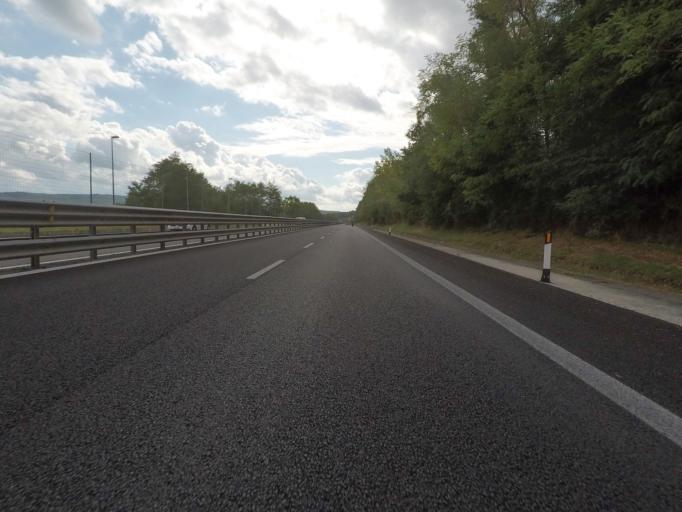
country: IT
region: Tuscany
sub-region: Provincia di Siena
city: Serre di Rapolano
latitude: 43.2629
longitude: 11.6301
